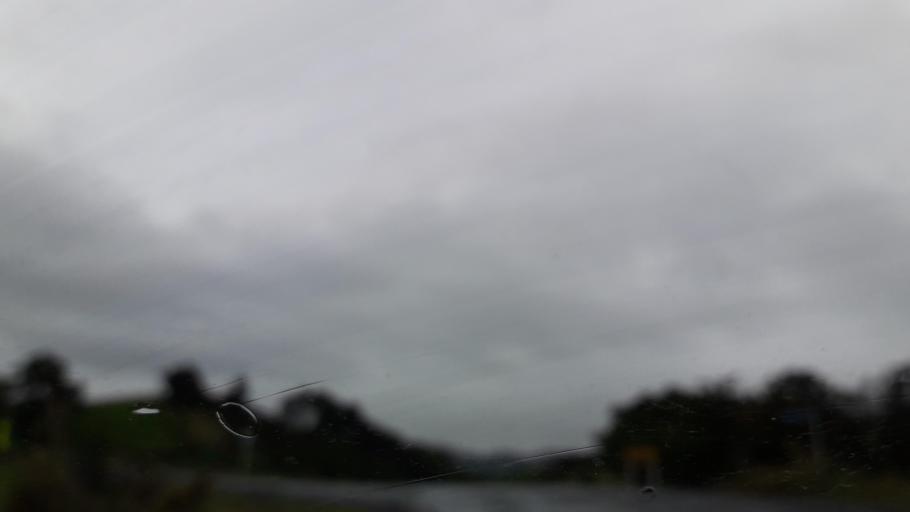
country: NZ
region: Northland
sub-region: Far North District
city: Kaitaia
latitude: -35.3571
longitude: 173.4907
